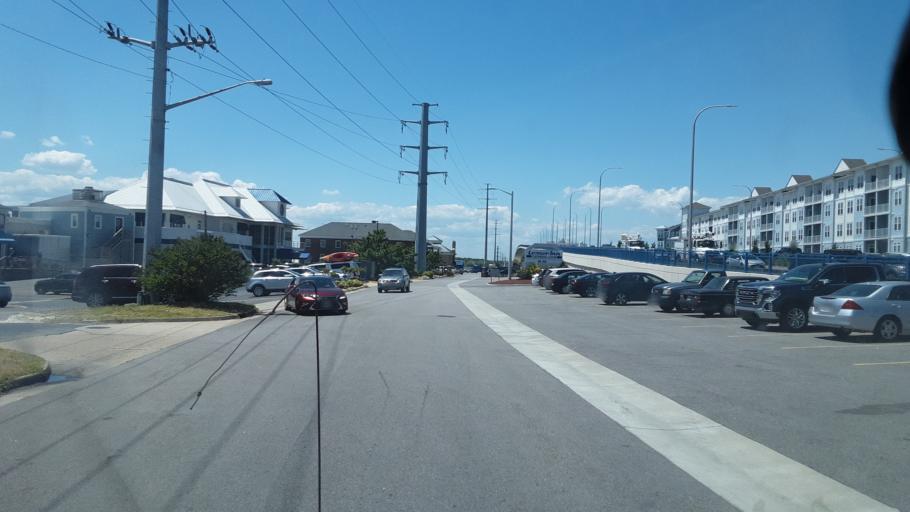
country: US
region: Virginia
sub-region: City of Virginia Beach
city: Virginia Beach
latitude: 36.9070
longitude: -76.0868
